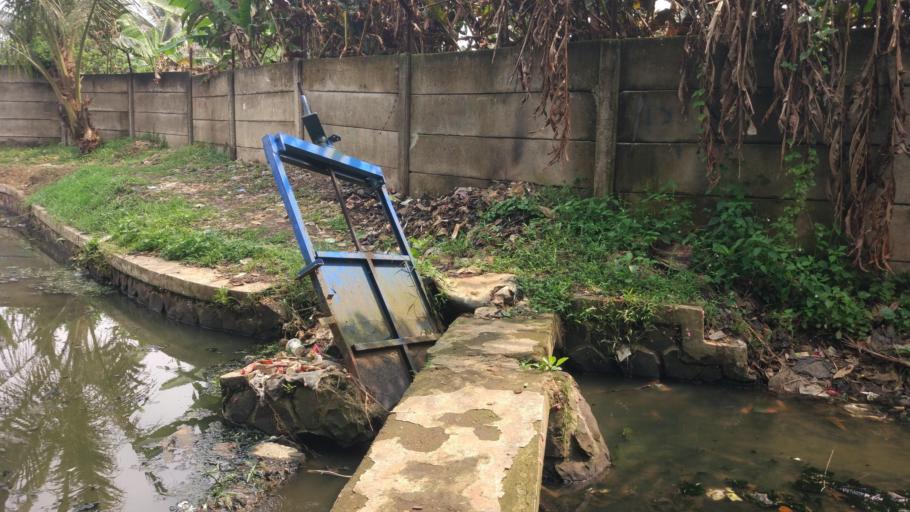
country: ID
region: West Java
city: Ciampea
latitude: -6.5648
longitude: 106.7169
